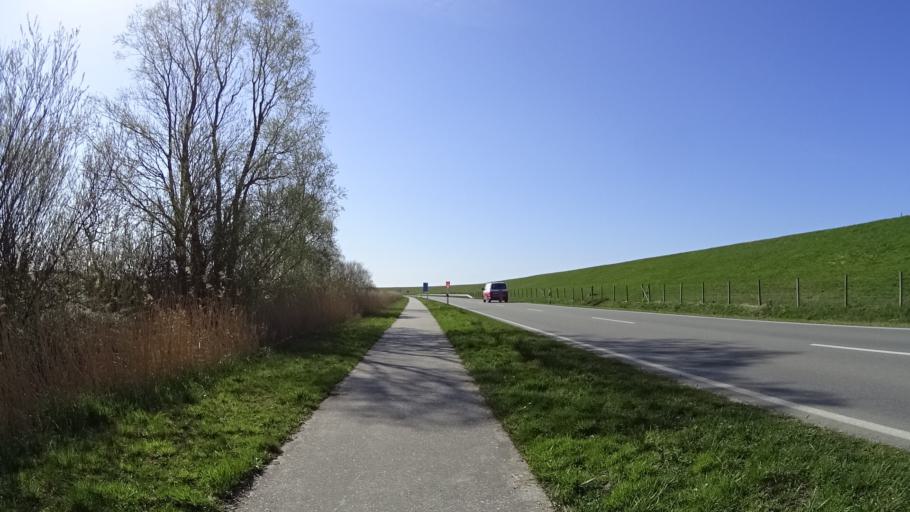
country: DE
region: Lower Saxony
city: Jemgum
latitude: 53.2408
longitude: 7.4073
